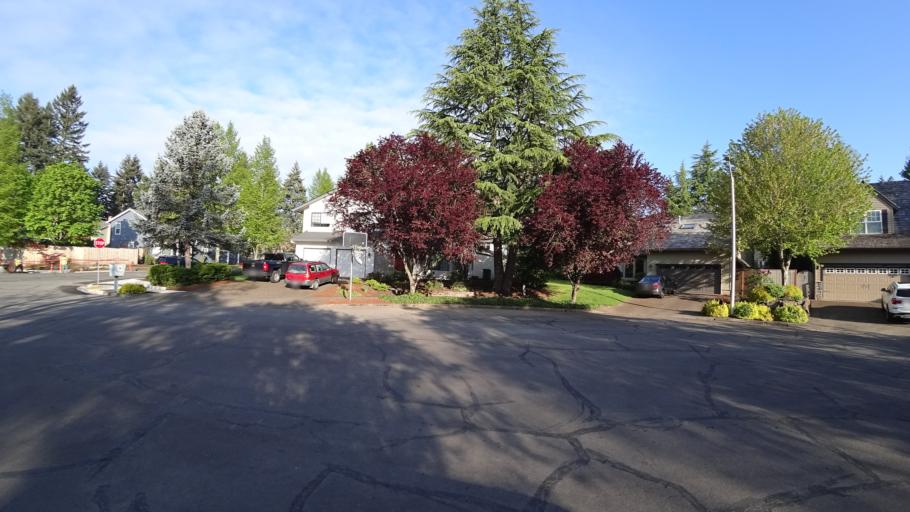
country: US
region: Oregon
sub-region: Washington County
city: Beaverton
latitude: 45.4474
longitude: -122.8185
